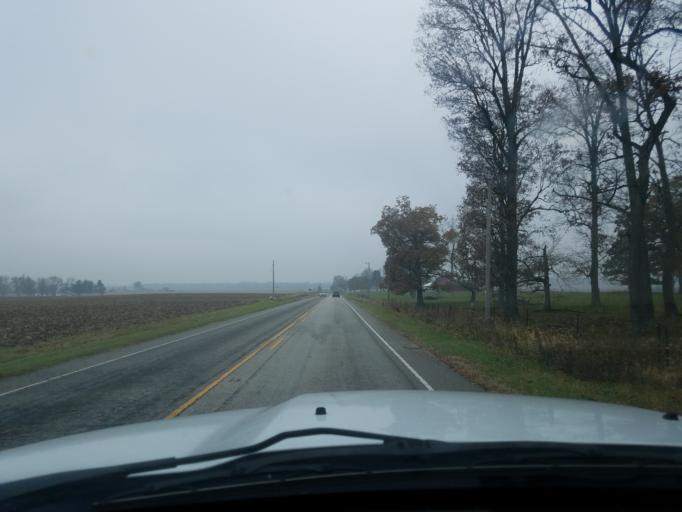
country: US
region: Indiana
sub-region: Cass County
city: Walton
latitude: 40.7577
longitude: -86.2000
